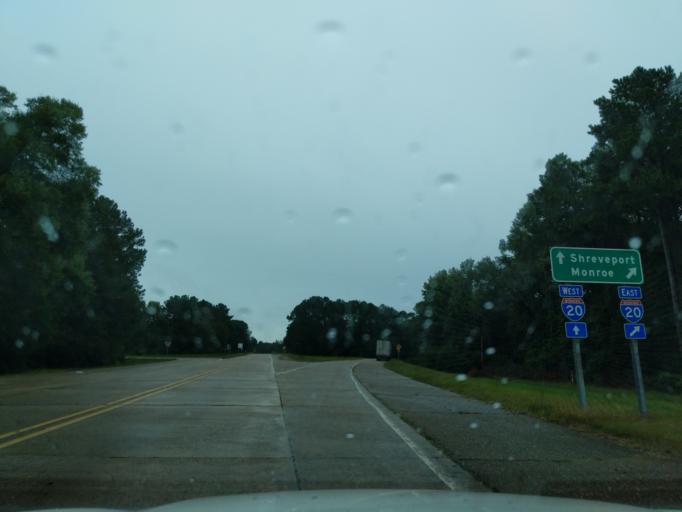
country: US
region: Louisiana
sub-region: Bienville Parish
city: Arcadia
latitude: 32.5604
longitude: -93.0542
